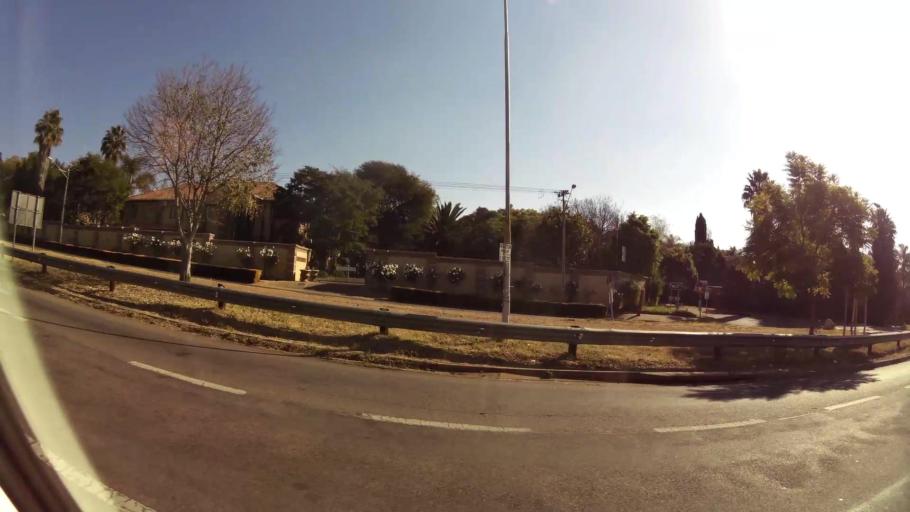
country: ZA
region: Gauteng
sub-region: City of Tshwane Metropolitan Municipality
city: Centurion
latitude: -25.8070
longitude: 28.2820
